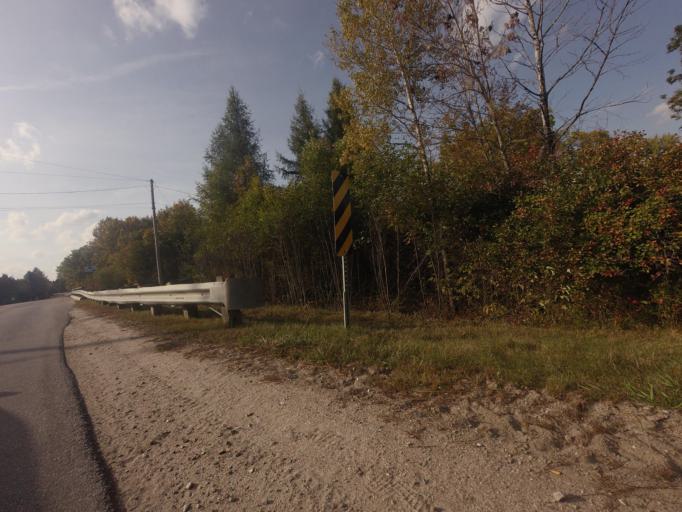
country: CA
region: Quebec
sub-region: Outaouais
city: Maniwaki
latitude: 46.3648
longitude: -75.9920
